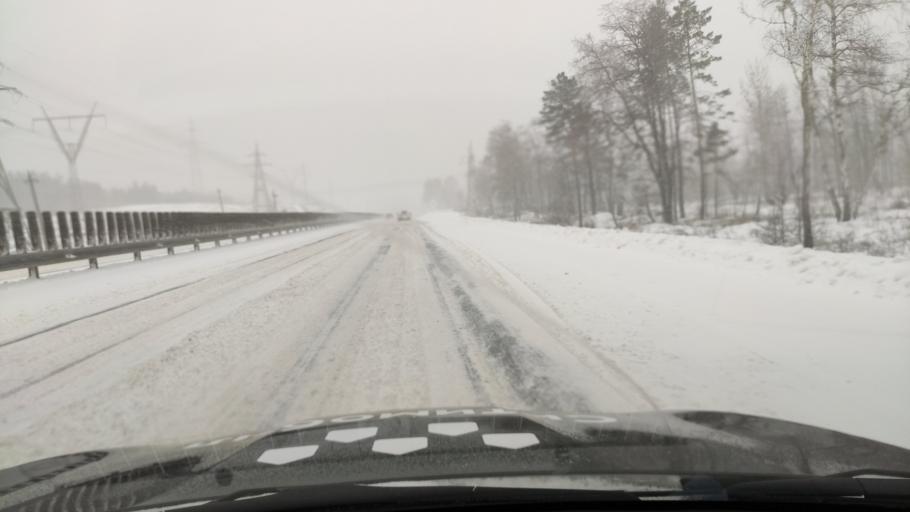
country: RU
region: Samara
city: Pribrezhnyy
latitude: 53.5129
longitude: 49.9121
